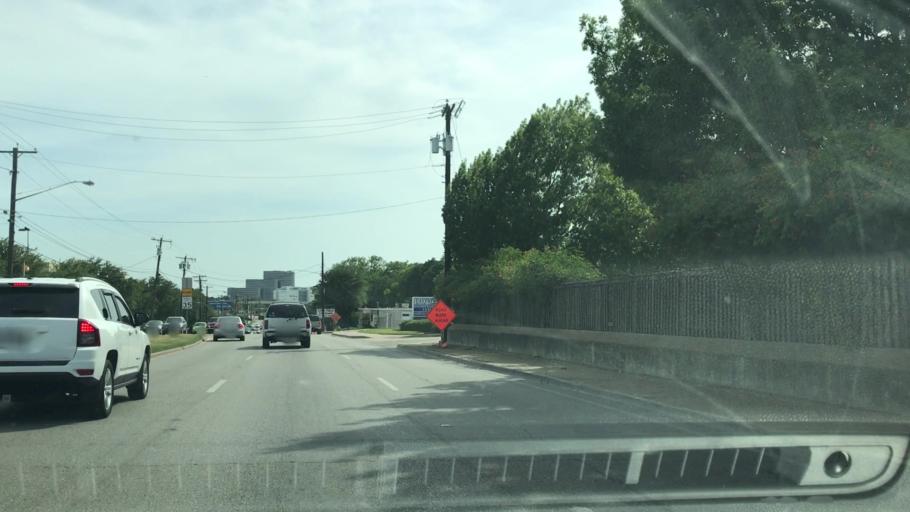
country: US
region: Texas
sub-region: Dallas County
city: Highland Park
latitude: 32.8209
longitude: -96.8371
